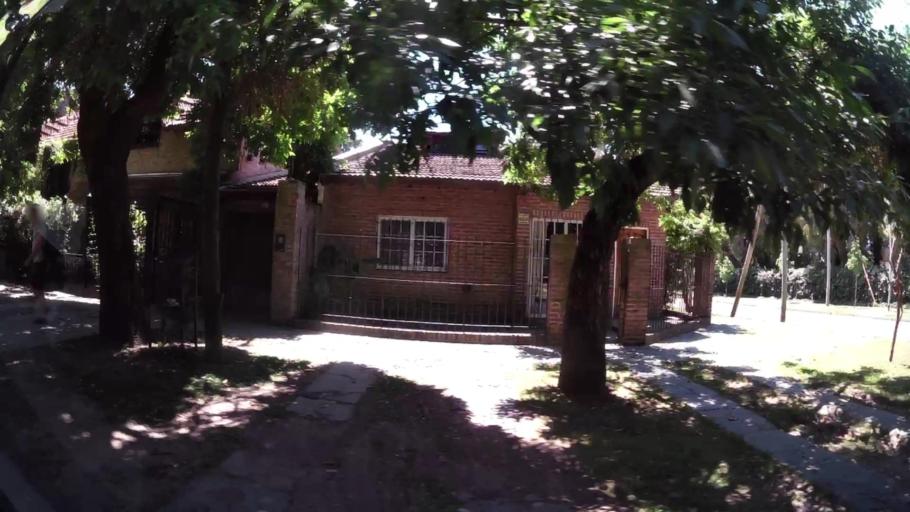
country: AR
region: Buenos Aires
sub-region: Partido de Tigre
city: Tigre
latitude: -34.4954
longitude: -58.6412
